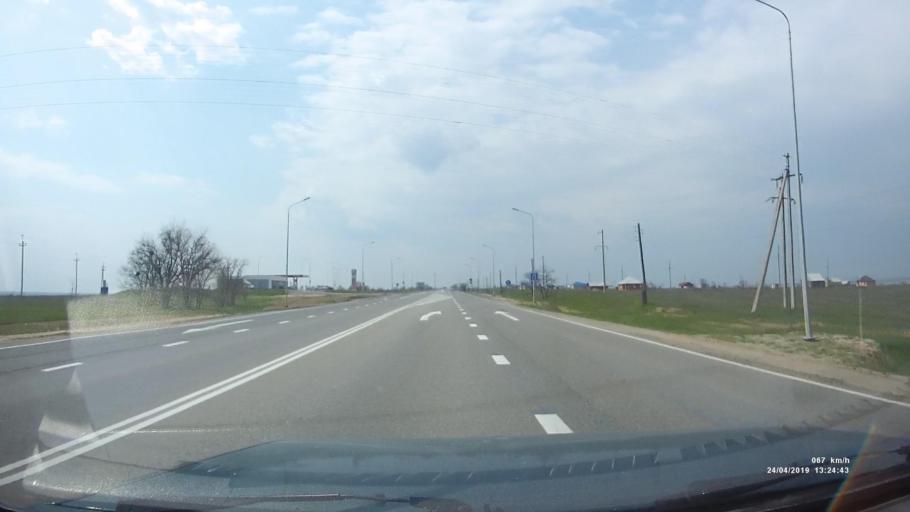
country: RU
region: Kalmykiya
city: Elista
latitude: 46.2848
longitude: 44.2507
